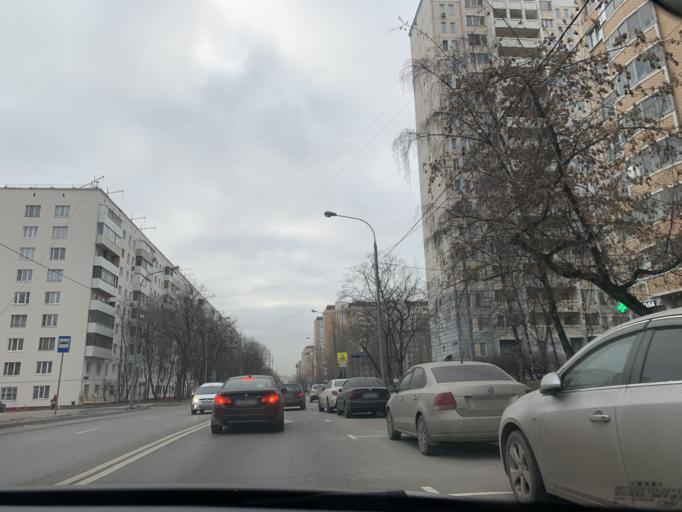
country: RU
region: Moskovskaya
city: Vostochnoe Degunino
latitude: 55.8729
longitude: 37.5591
